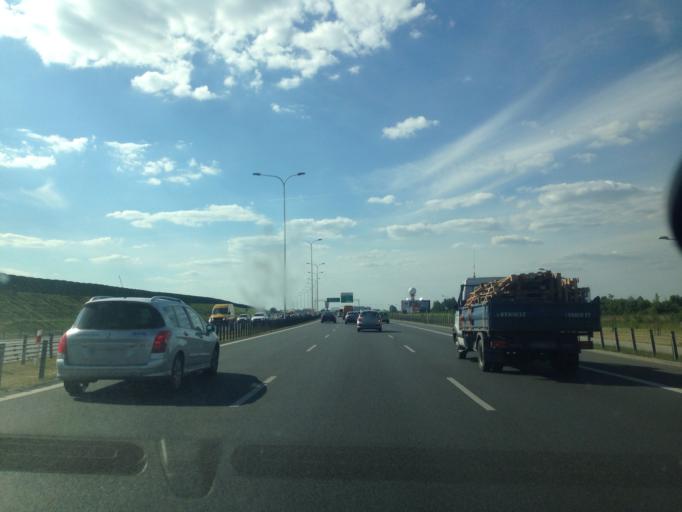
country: PL
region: Masovian Voivodeship
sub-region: Powiat pruszkowski
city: Rybie
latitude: 52.1586
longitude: 20.9537
